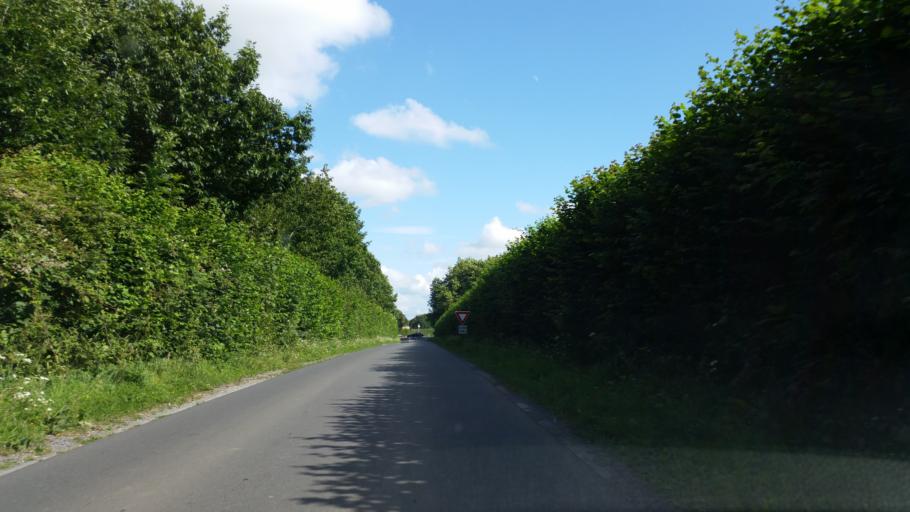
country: FR
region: Lower Normandy
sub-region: Departement du Calvados
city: Bavent
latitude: 49.2397
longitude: -0.1919
